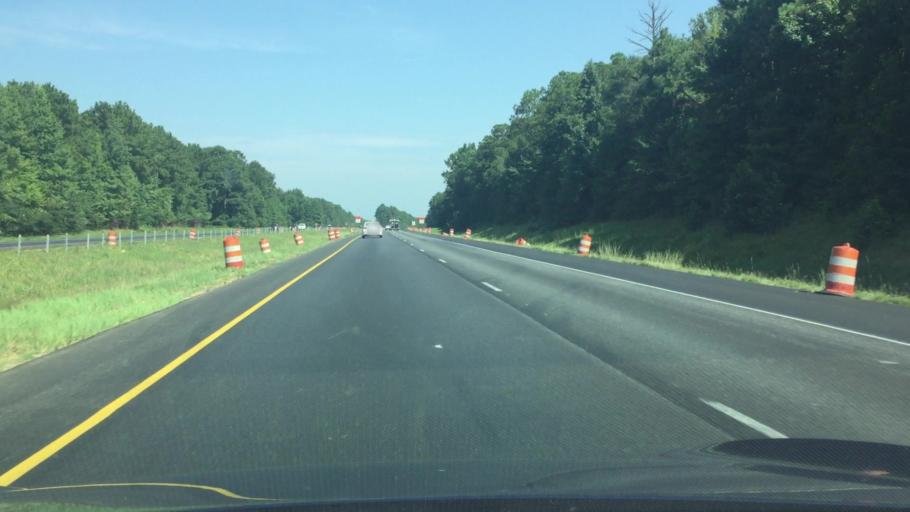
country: US
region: Alabama
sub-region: Chilton County
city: Clanton
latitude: 32.7627
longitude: -86.5607
